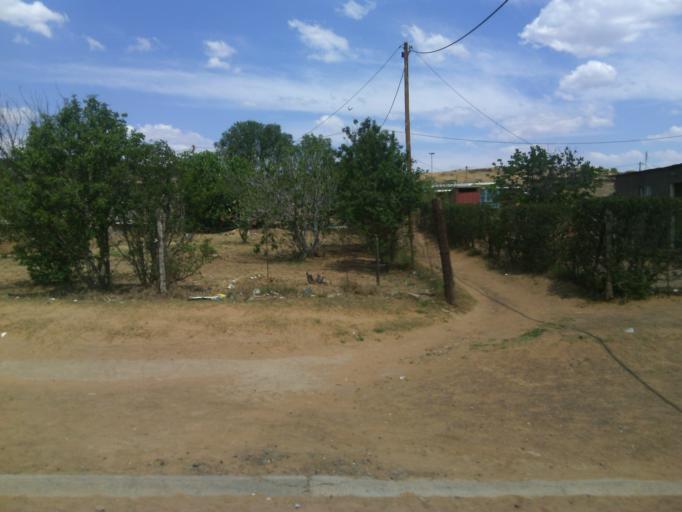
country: ZA
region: Orange Free State
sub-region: Xhariep District Municipality
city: Dewetsdorp
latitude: -29.5782
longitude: 26.6800
